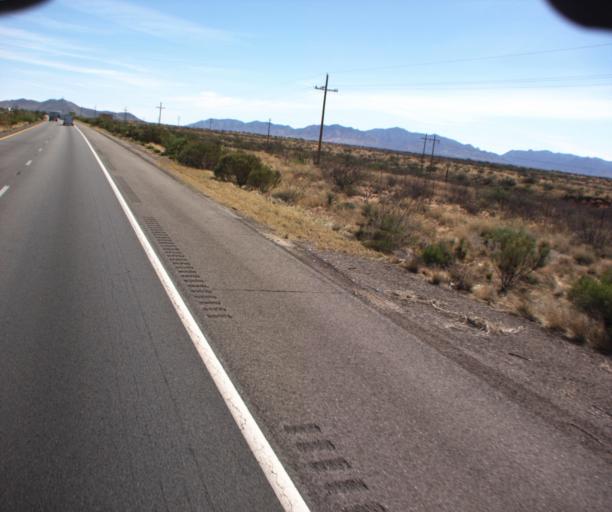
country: US
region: Arizona
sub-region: Cochise County
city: Saint David
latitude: 31.9855
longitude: -110.1956
